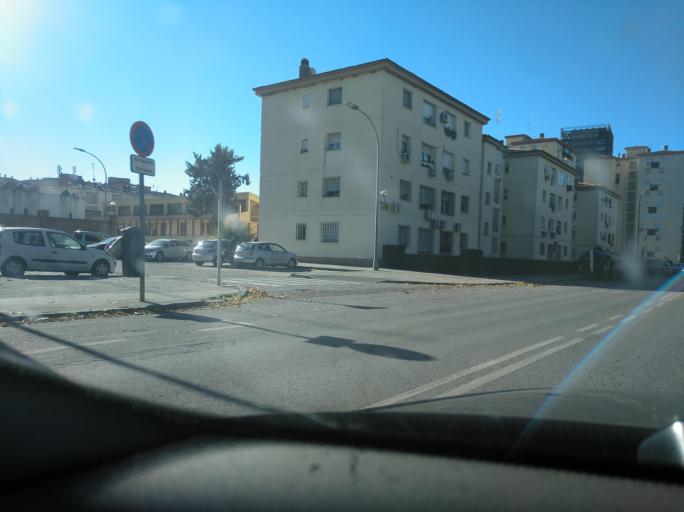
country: ES
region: Extremadura
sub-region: Provincia de Badajoz
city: Badajoz
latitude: 38.8759
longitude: -6.9867
